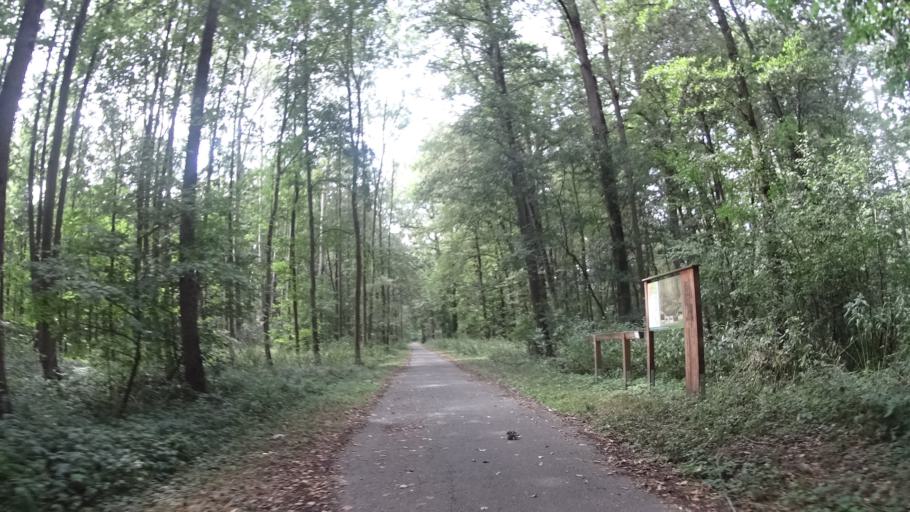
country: CZ
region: Olomoucky
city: Skrben
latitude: 49.6597
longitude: 17.1915
